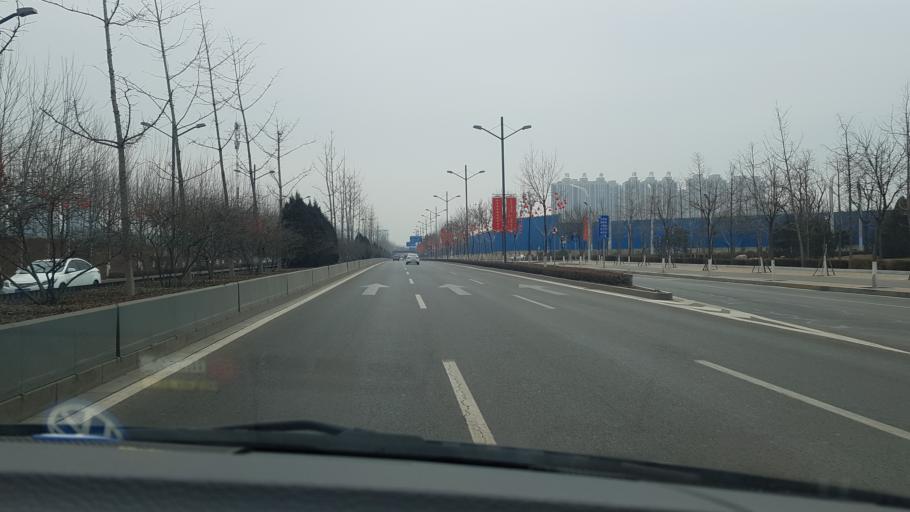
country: CN
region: Shanxi Sheng
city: Qianfeng
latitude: 37.8011
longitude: 112.5308
